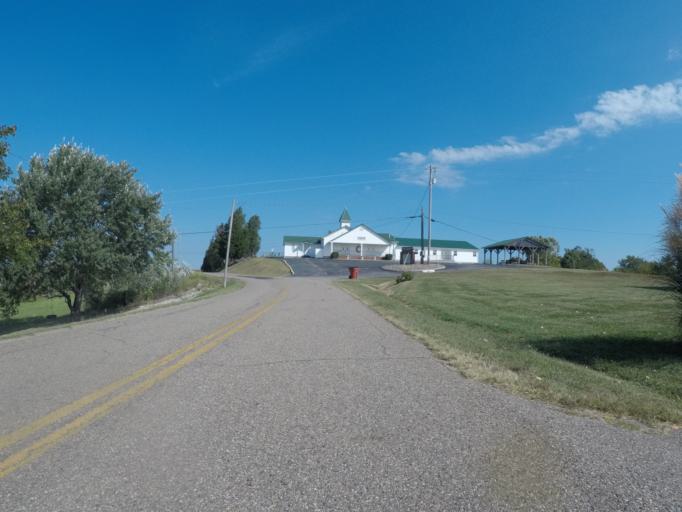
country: US
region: West Virginia
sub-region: Cabell County
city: Lesage
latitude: 38.6502
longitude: -82.4206
